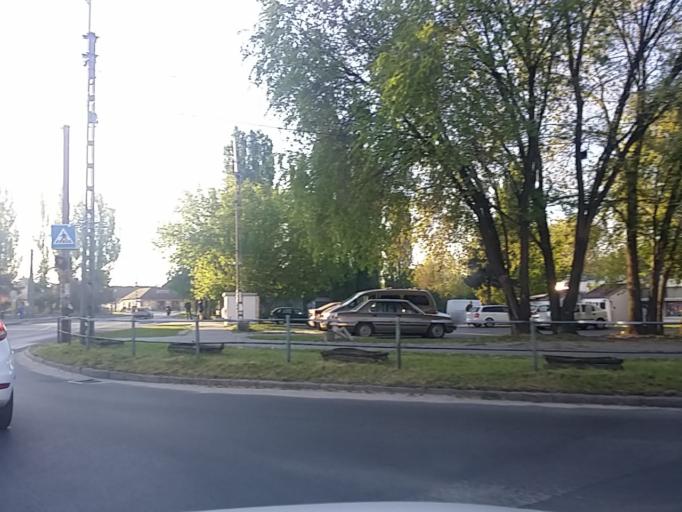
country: HU
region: Pest
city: Fot
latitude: 47.6072
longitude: 19.1973
